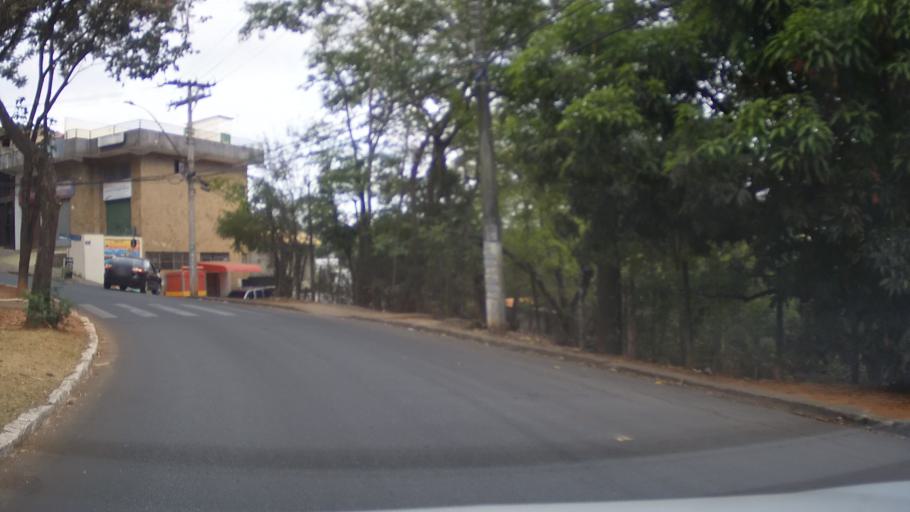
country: BR
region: Minas Gerais
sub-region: Belo Horizonte
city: Belo Horizonte
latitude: -19.8194
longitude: -43.9686
